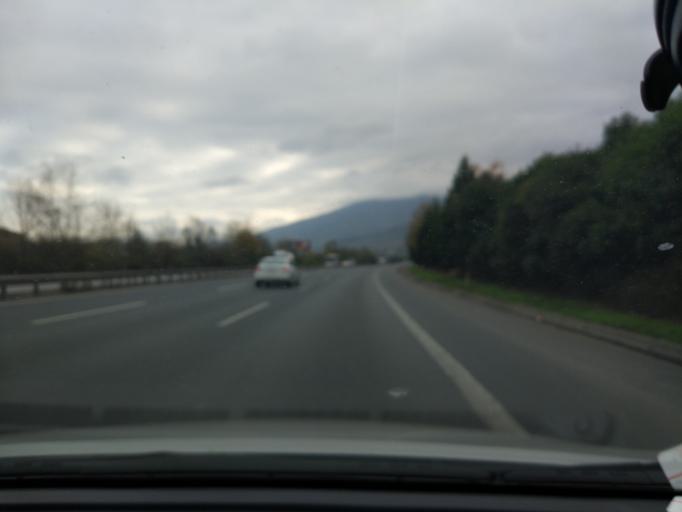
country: TR
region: Kocaeli
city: Derbent
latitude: 40.7205
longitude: 30.1081
